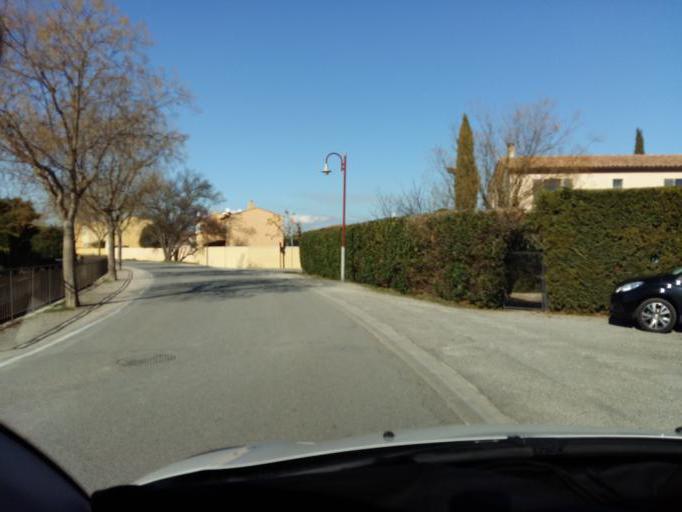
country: FR
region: Provence-Alpes-Cote d'Azur
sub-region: Departement du Vaucluse
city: Cheval-Blanc
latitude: 43.8019
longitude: 5.0625
